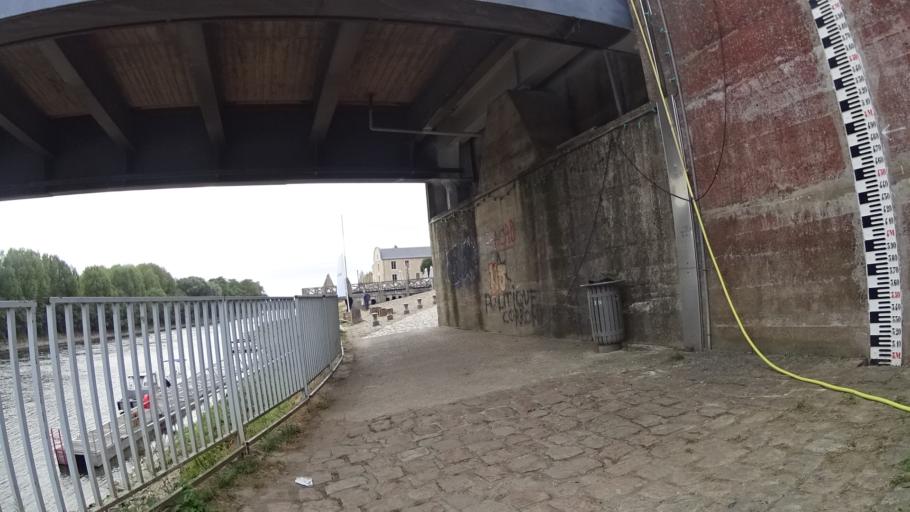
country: FR
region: Pays de la Loire
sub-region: Departement de Maine-et-Loire
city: Saint-Florent-le-Vieil
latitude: 47.3643
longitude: -1.0146
